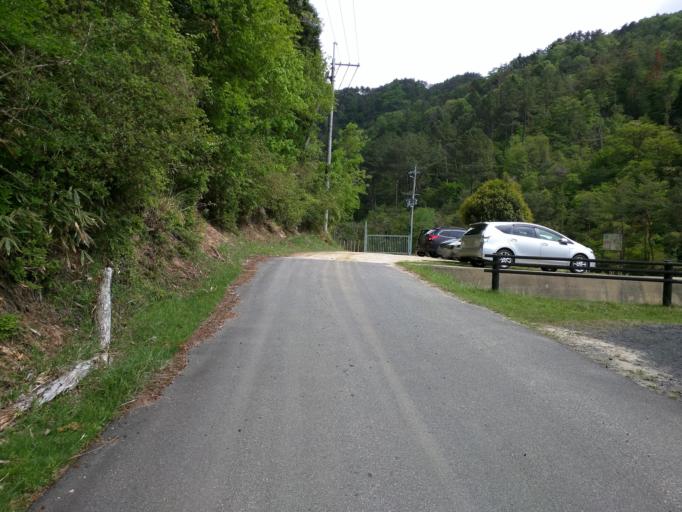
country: JP
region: Mie
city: Ueno-ebisumachi
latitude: 34.8262
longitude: 135.9956
